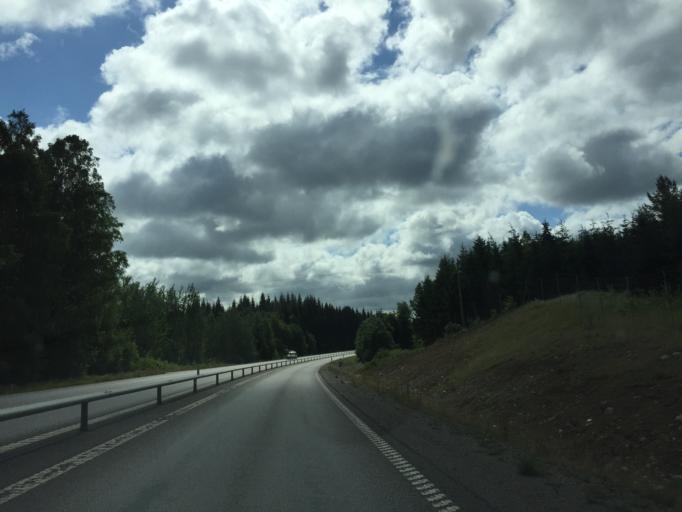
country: SE
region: OErebro
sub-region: Lekebergs Kommun
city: Fjugesta
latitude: 59.2624
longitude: 14.8065
